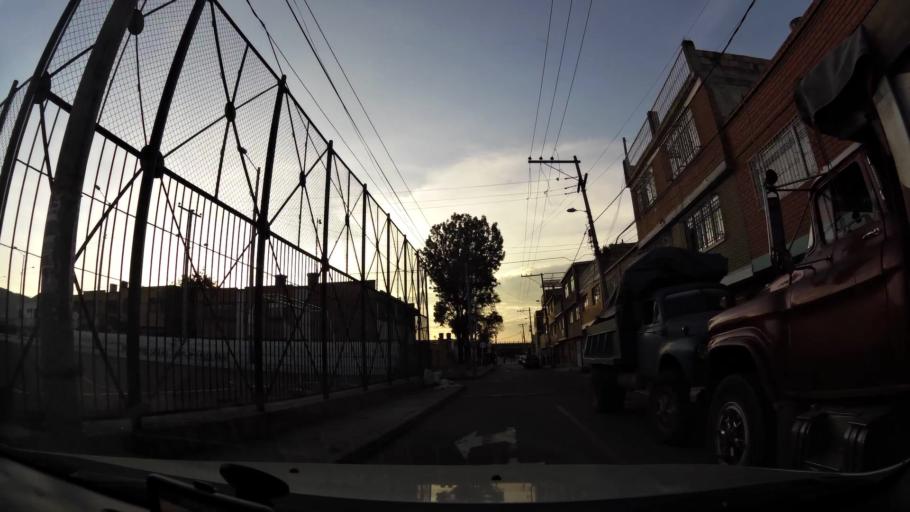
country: CO
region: Bogota D.C.
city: Bogota
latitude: 4.5662
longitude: -74.1363
